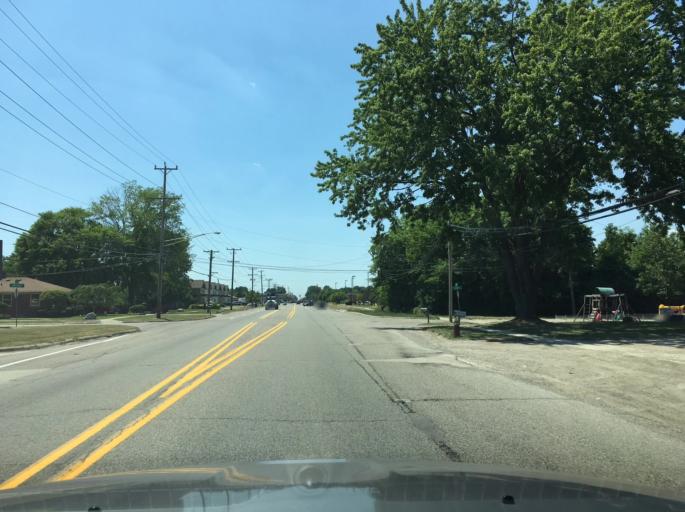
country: US
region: Michigan
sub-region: Macomb County
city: Clinton
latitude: 42.5548
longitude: -82.8940
